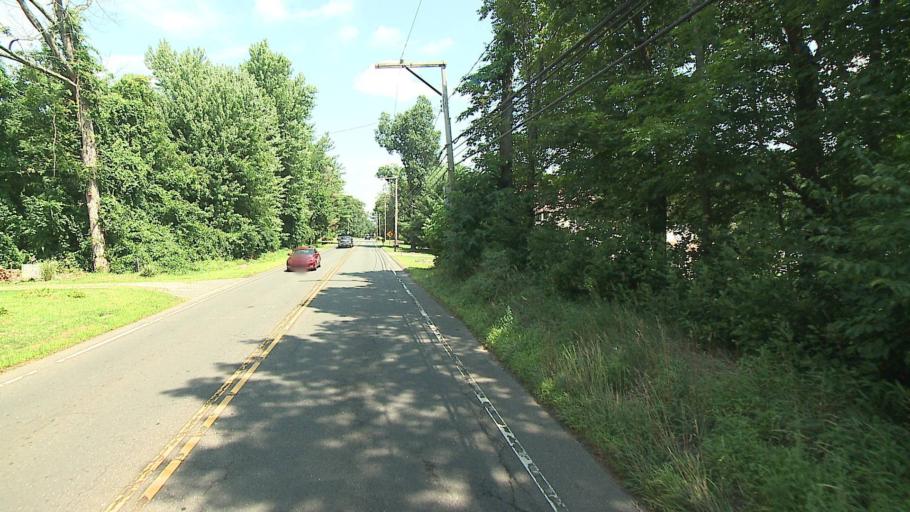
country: US
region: Connecticut
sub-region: Hartford County
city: Farmington
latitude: 41.7375
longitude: -72.8911
